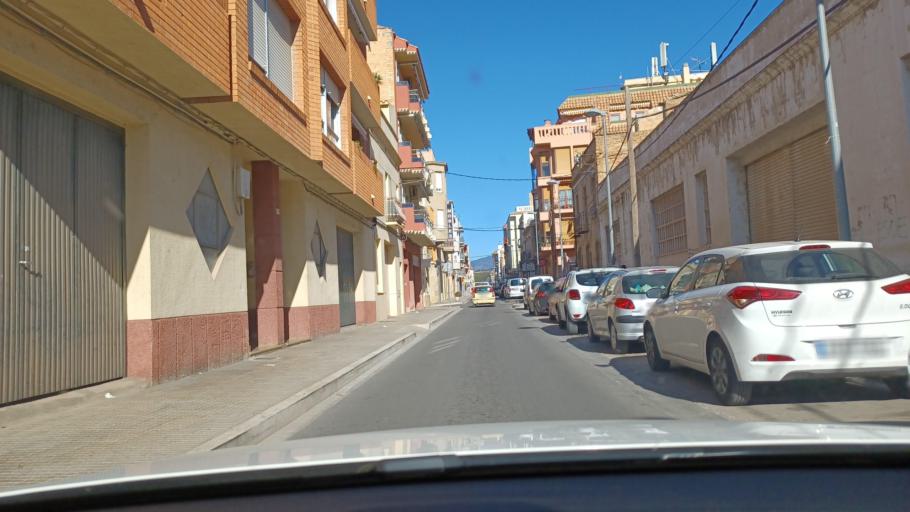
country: ES
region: Catalonia
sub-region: Provincia de Tarragona
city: Tortosa
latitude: 40.8165
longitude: 0.5226
